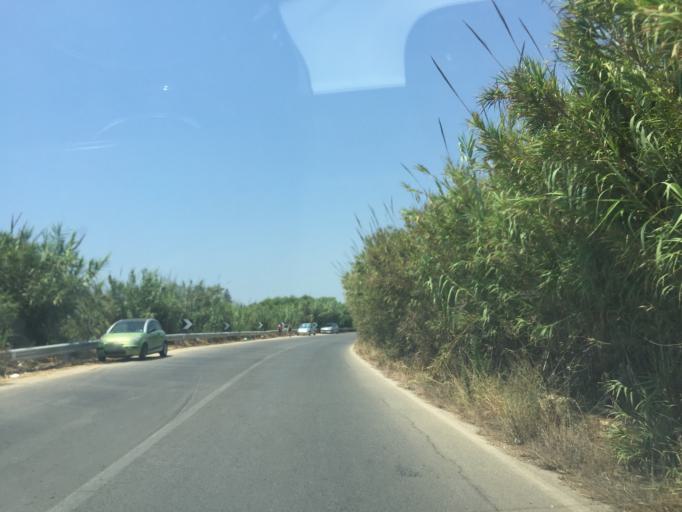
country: IT
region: Sicily
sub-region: Ragusa
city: Donnalucata
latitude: 36.7692
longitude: 14.6121
